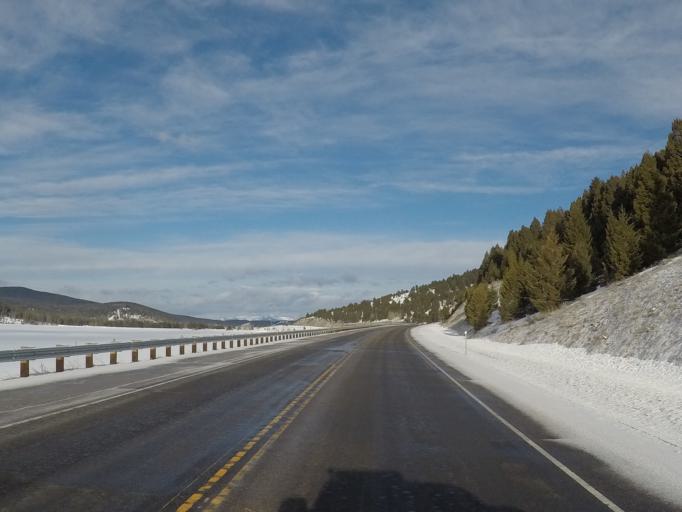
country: US
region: Montana
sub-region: Granite County
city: Philipsburg
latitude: 46.1685
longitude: -113.2217
